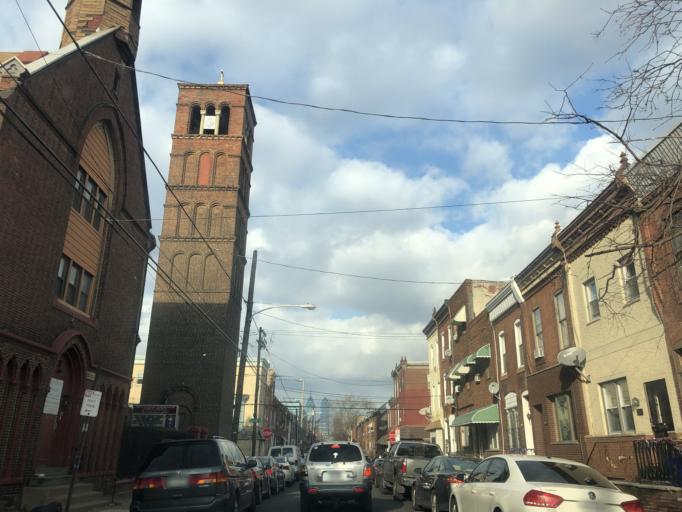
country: US
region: Pennsylvania
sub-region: Philadelphia County
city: Philadelphia
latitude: 39.9267
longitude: -75.1725
